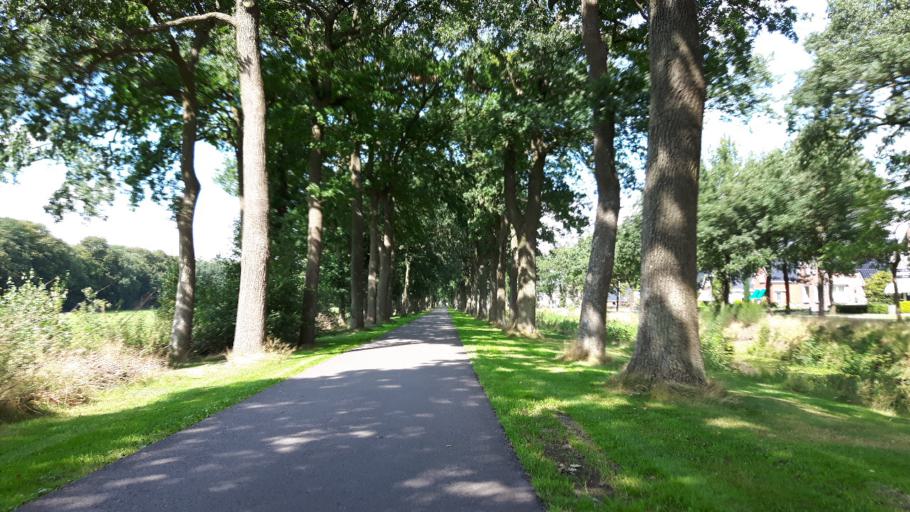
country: NL
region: Friesland
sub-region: Gemeente Smallingerland
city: Drachtstercompagnie
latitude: 53.0765
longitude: 6.2612
